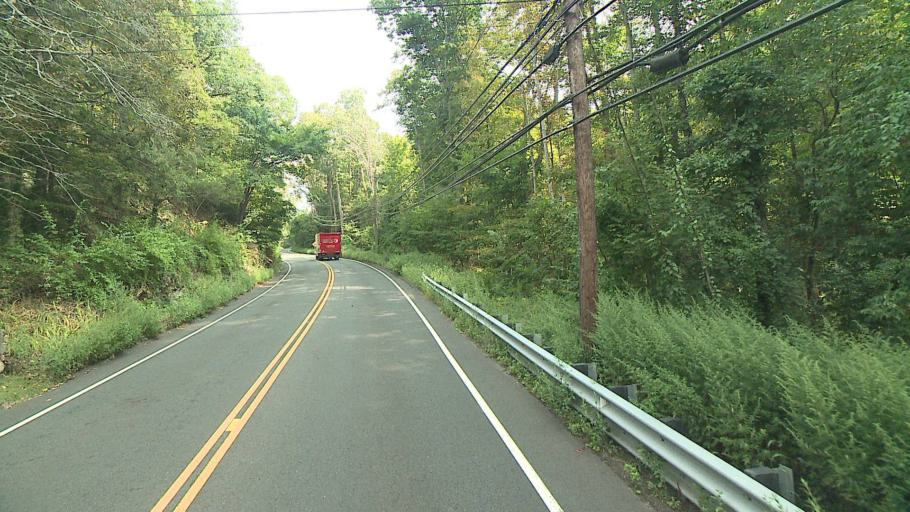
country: US
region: Connecticut
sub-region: Fairfield County
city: Georgetown
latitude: 41.2974
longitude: -73.3890
